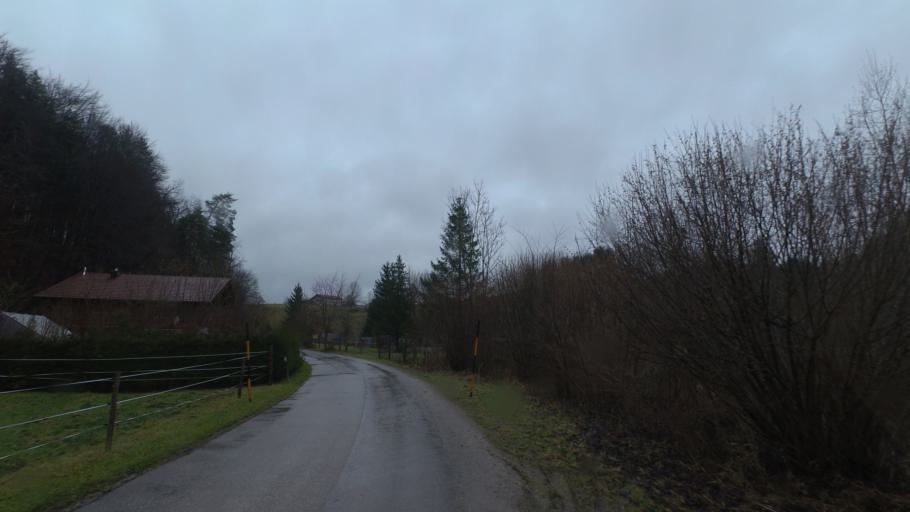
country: DE
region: Bavaria
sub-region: Upper Bavaria
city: Nussdorf
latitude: 47.9172
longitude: 12.6285
